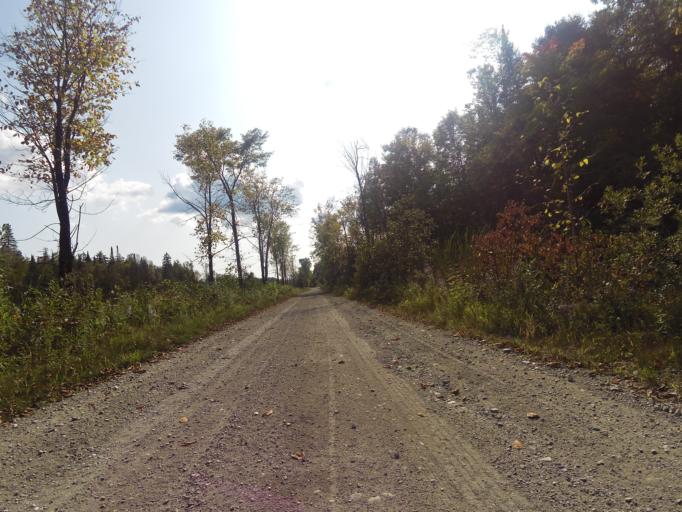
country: CA
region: Ontario
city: Renfrew
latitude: 45.1264
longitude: -76.6883
